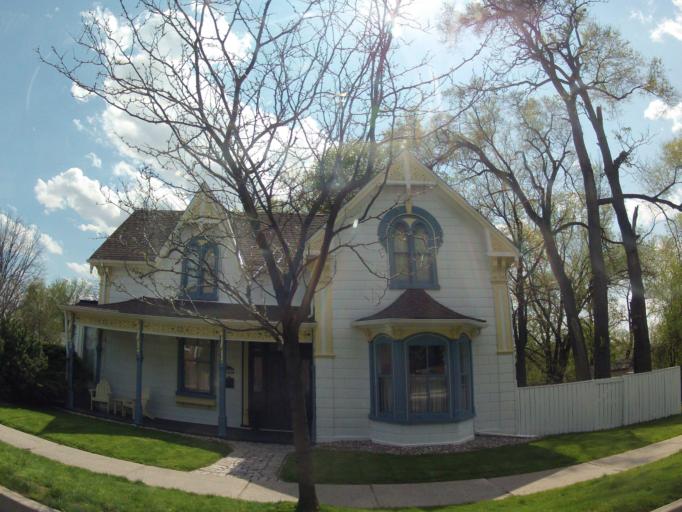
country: CA
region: Ontario
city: Mississauga
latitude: 43.5790
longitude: -79.7100
